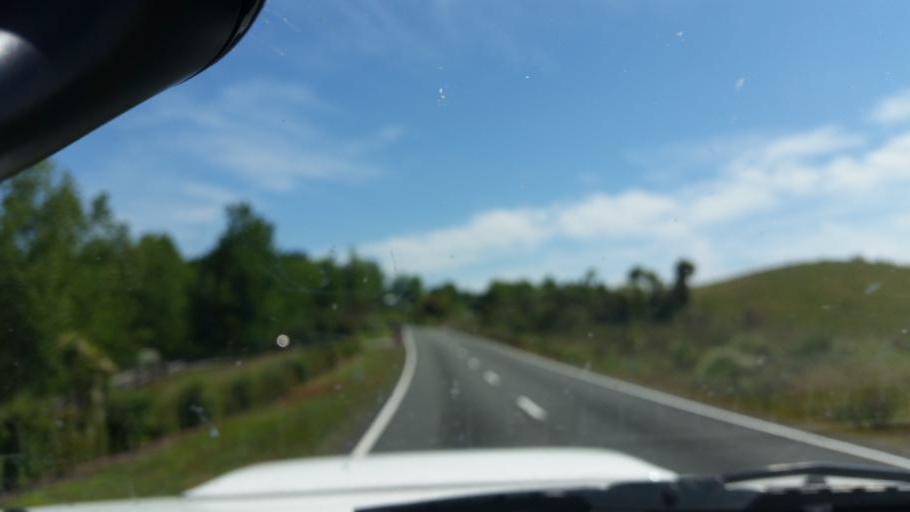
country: NZ
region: Auckland
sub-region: Auckland
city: Wellsford
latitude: -36.2157
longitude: 174.3897
